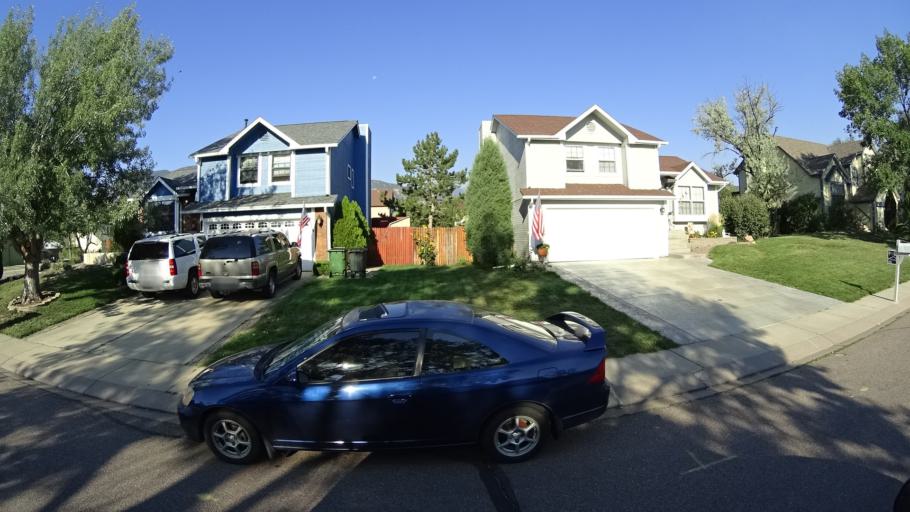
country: US
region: Colorado
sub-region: El Paso County
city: Stratmoor
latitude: 38.7738
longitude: -104.7994
